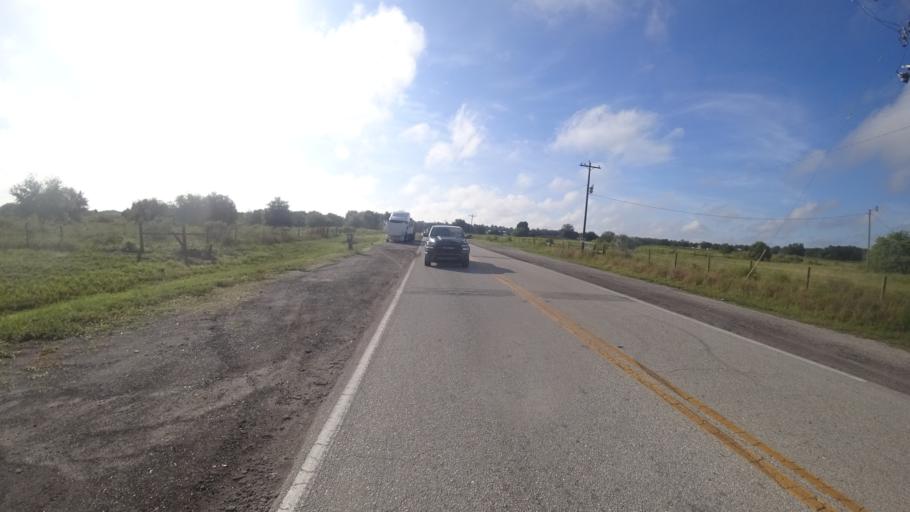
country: US
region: Florida
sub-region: Sarasota County
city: The Meadows
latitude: 27.4743
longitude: -82.3067
